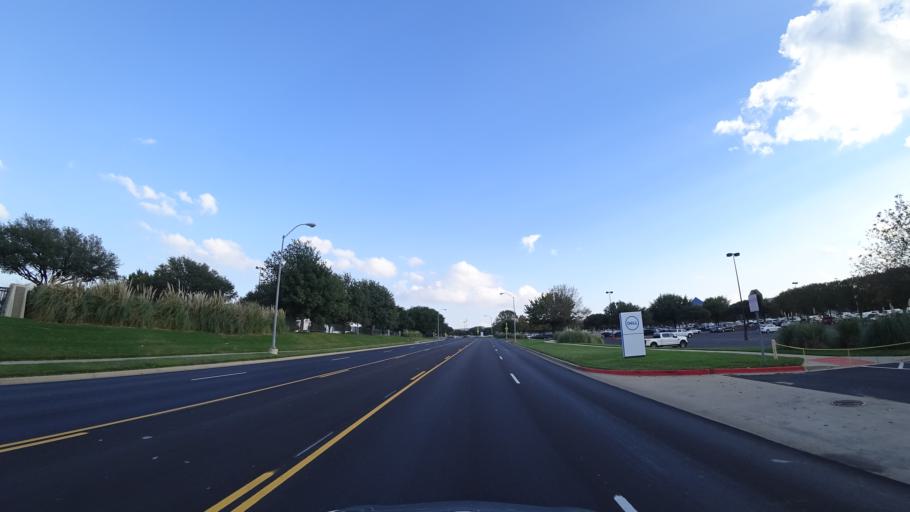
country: US
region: Texas
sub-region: Williamson County
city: Round Rock
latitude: 30.4867
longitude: -97.6666
